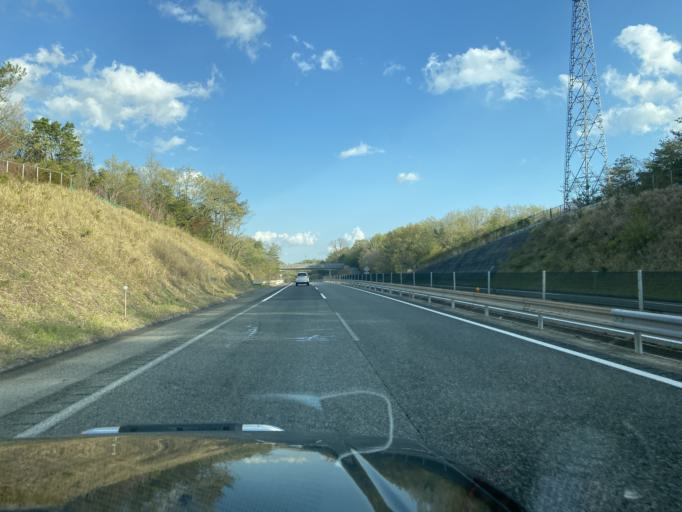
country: JP
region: Hyogo
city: Sandacho
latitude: 34.9512
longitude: 135.1395
